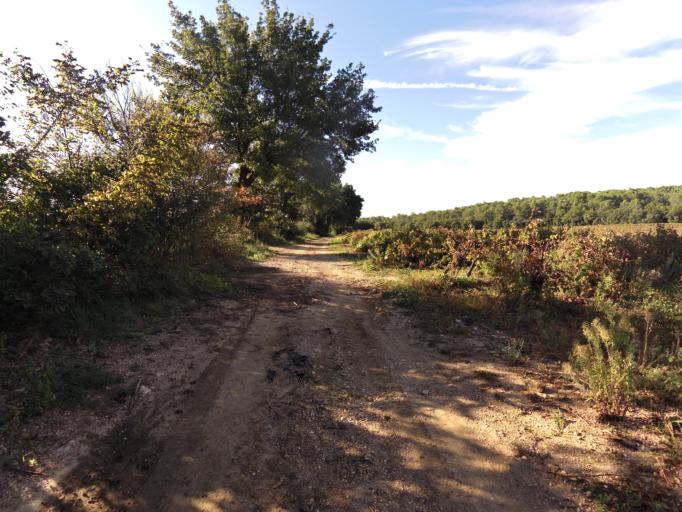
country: FR
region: Languedoc-Roussillon
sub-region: Departement du Gard
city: Sommieres
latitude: 43.8103
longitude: 4.0843
